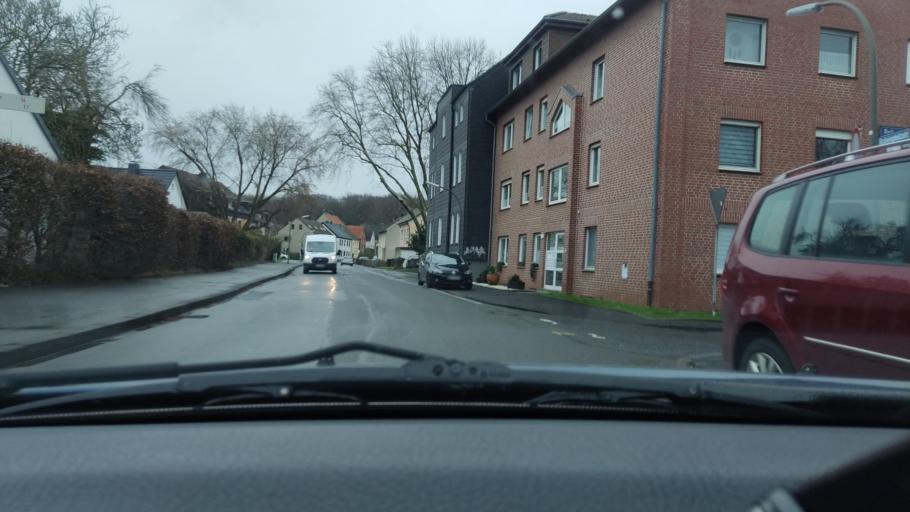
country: DE
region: North Rhine-Westphalia
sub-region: Regierungsbezirk Arnsberg
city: Dortmund
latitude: 51.5551
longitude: 7.4514
